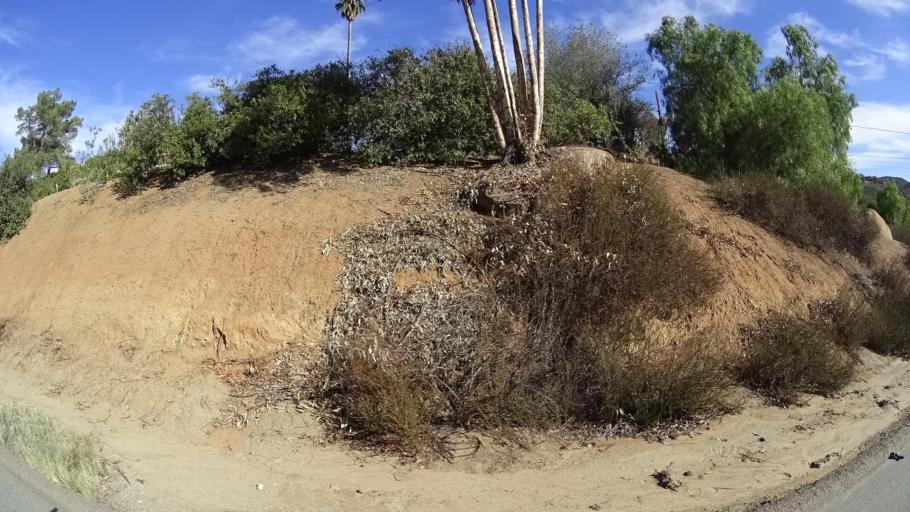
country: US
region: California
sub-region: San Diego County
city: Alpine
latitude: 32.8179
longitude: -116.7455
